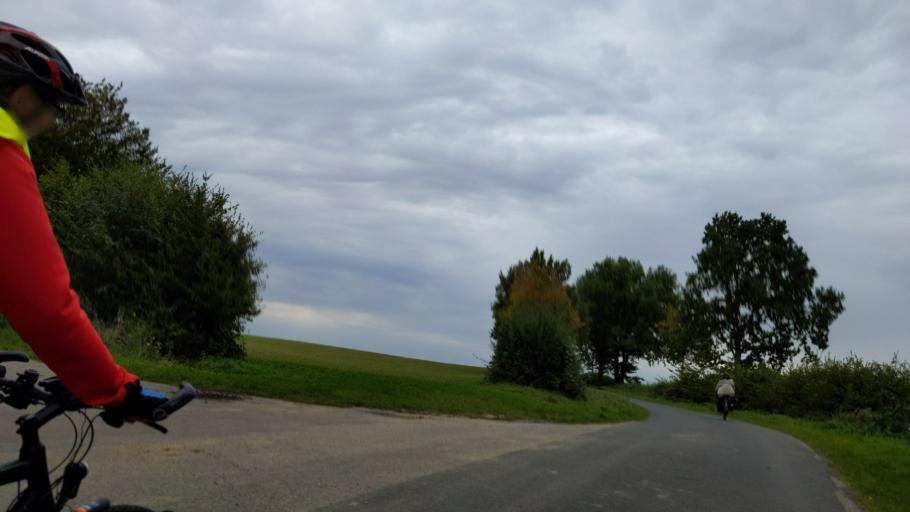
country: DE
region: Schleswig-Holstein
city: Bak
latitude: 53.7301
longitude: 10.7798
